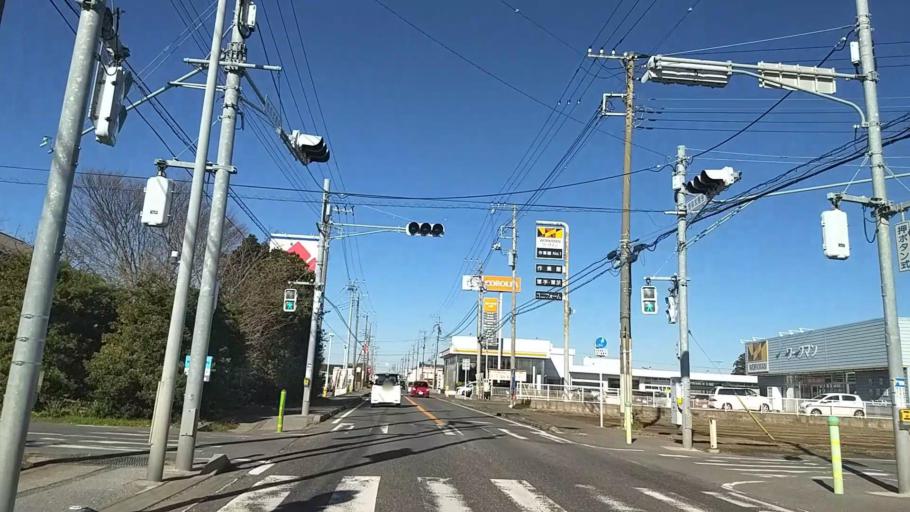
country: JP
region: Chiba
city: Ohara
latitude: 35.2688
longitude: 140.3940
